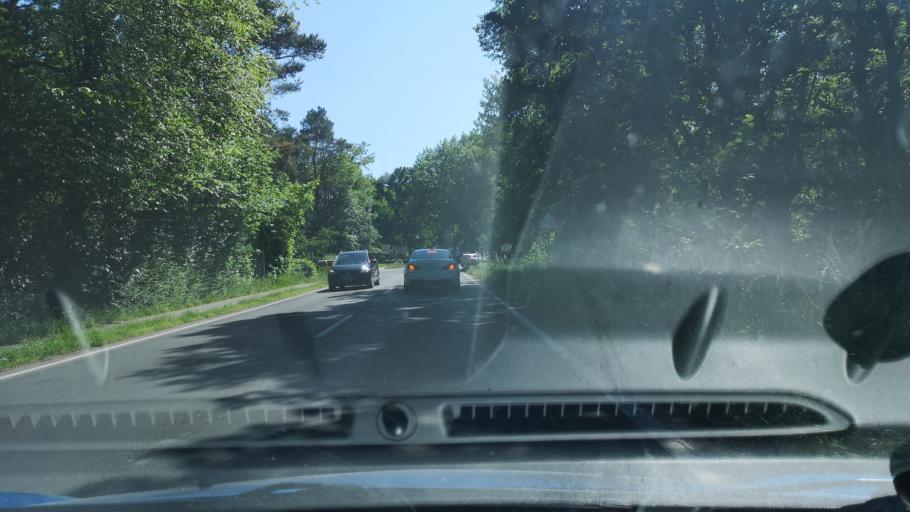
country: DE
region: Lower Saxony
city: Neustadt am Rubenberge
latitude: 52.4678
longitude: 9.4379
